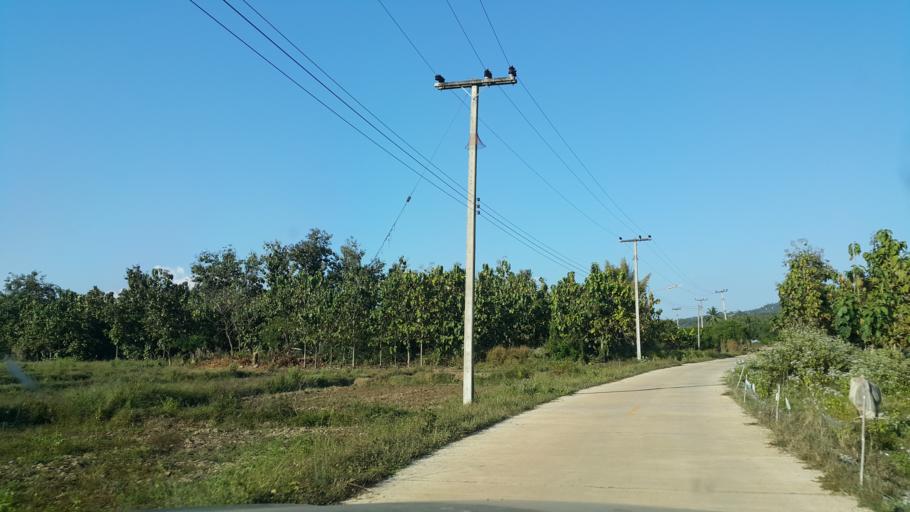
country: TH
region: Sukhothai
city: Thung Saliam
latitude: 17.3796
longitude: 99.5224
